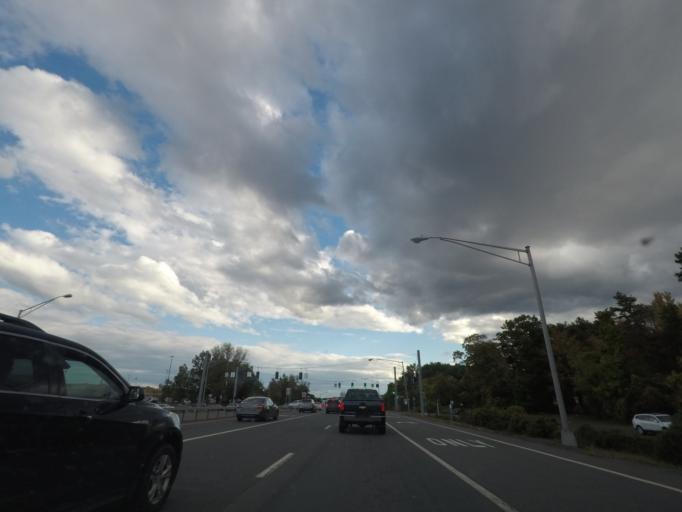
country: US
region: New York
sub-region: Albany County
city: McKownville
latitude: 42.6968
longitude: -73.8500
